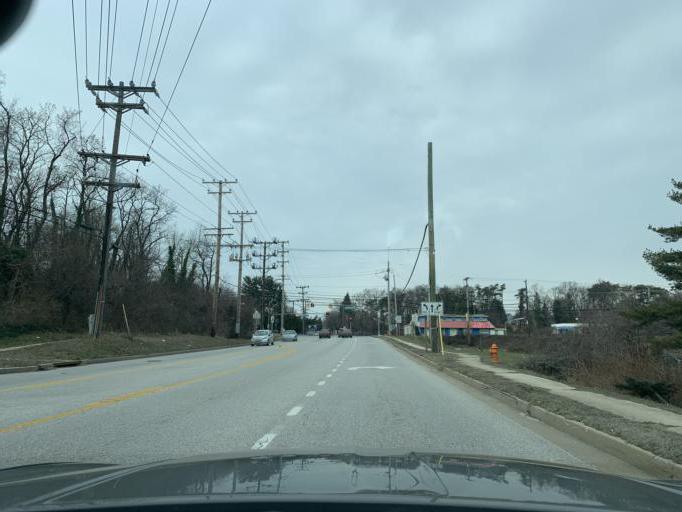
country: US
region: Maryland
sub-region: Howard County
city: Savage
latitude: 39.1156
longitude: -76.8302
